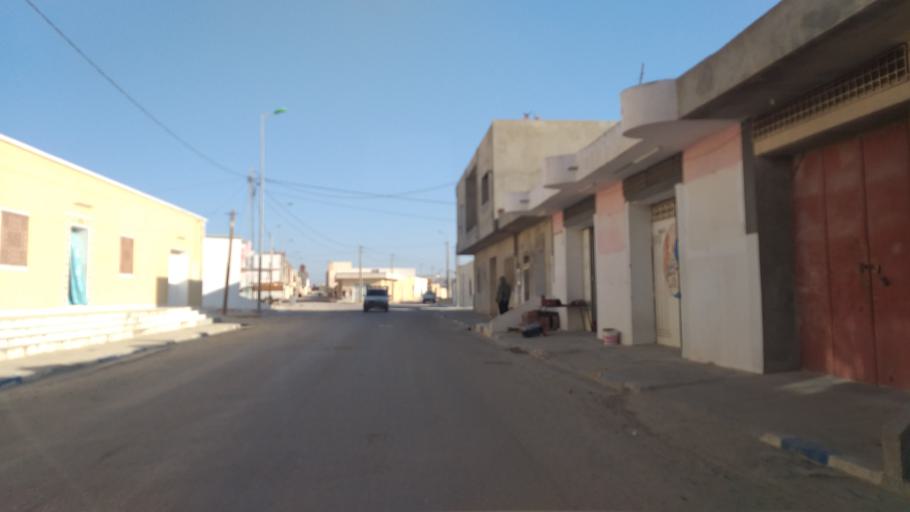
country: TN
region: Al Mahdiyah
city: El Jem
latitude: 35.2867
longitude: 10.7098
